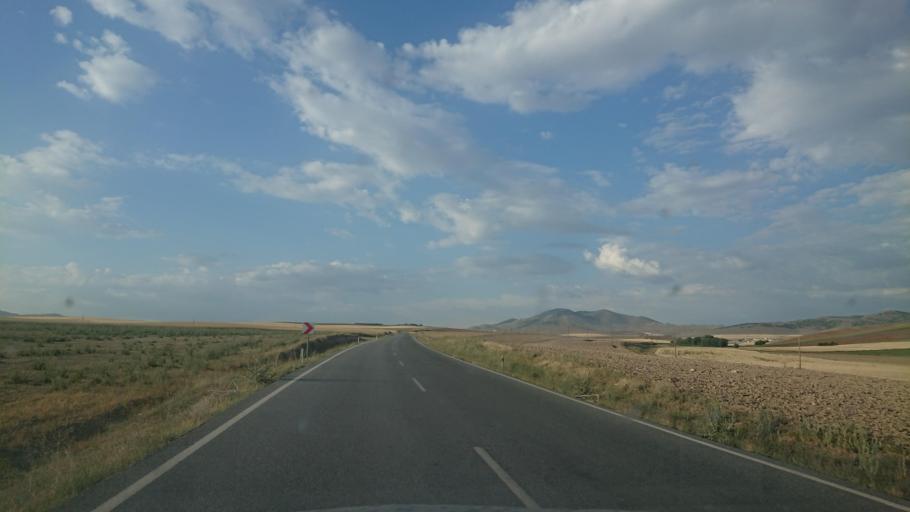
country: TR
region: Aksaray
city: Aksaray
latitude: 38.4887
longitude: 34.0688
